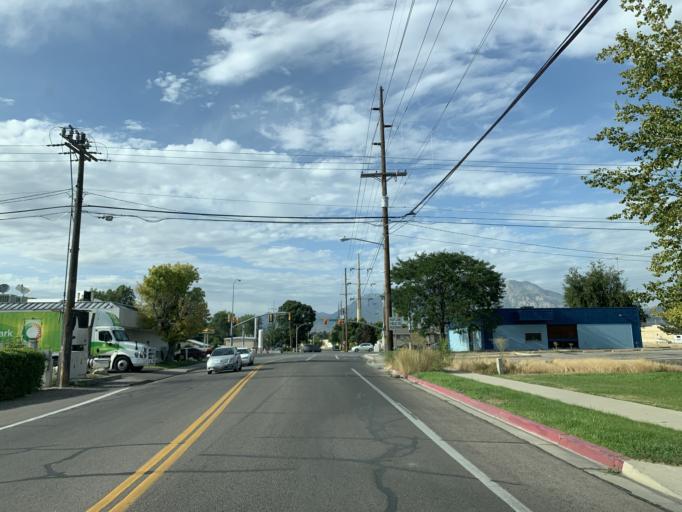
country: US
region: Utah
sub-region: Utah County
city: Provo
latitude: 40.2331
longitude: -111.6874
